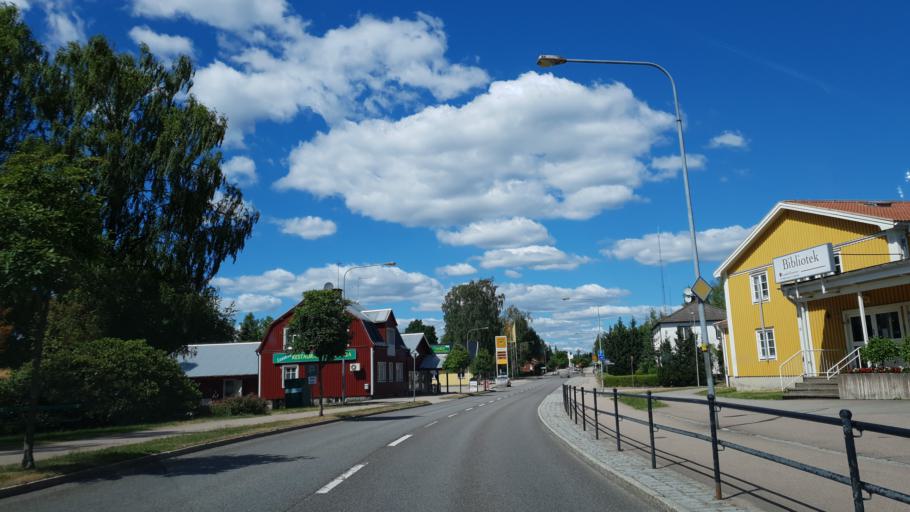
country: SE
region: Kronoberg
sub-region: Lessebo Kommun
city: Lessebo
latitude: 56.7552
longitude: 15.2674
